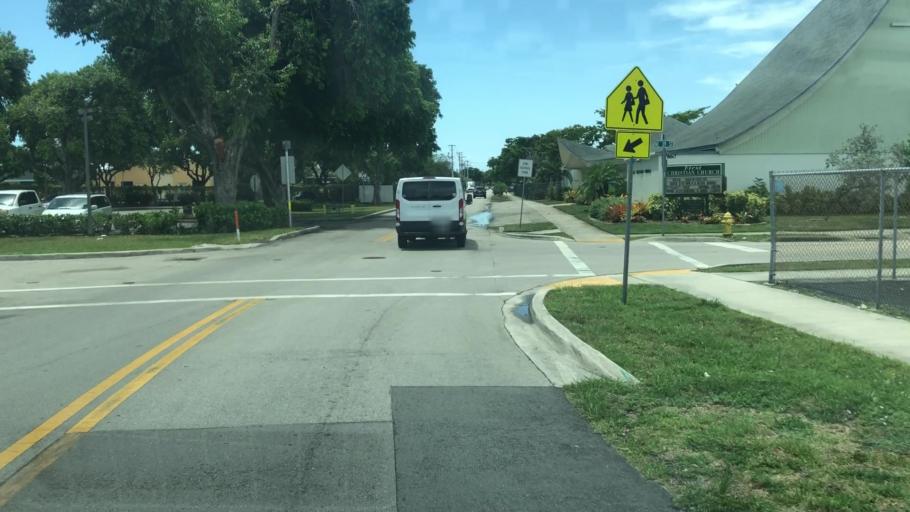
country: US
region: Florida
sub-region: Broward County
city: Pompano Beach Highlands
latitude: 26.2790
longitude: -80.0980
